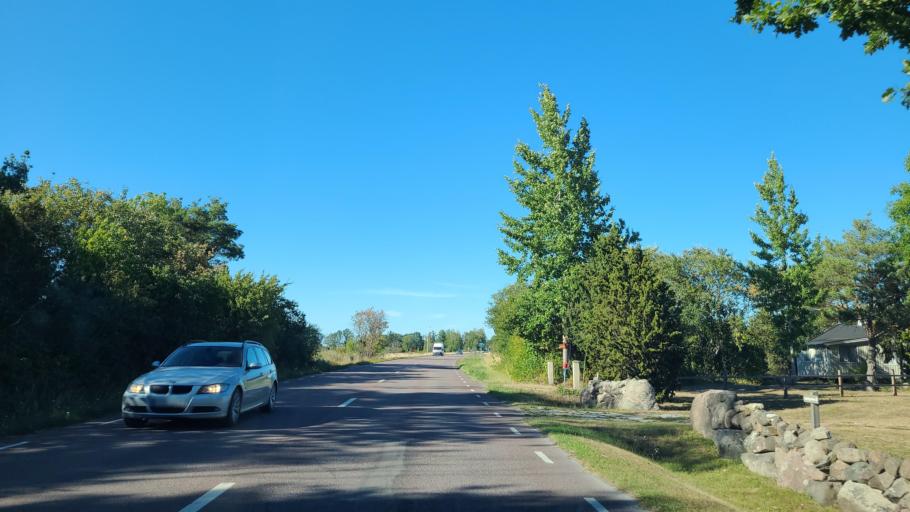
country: SE
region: Kalmar
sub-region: Borgholms Kommun
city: Borgholm
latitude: 57.2094
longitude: 17.0451
